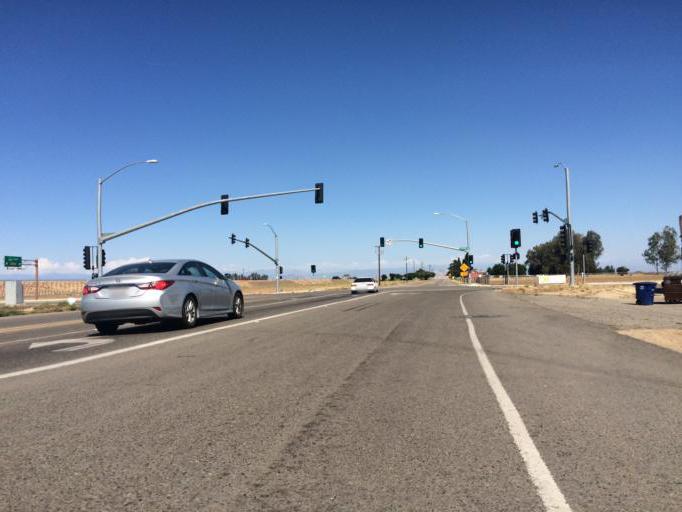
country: US
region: California
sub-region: Fresno County
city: Sunnyside
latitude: 36.7369
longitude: -119.6648
